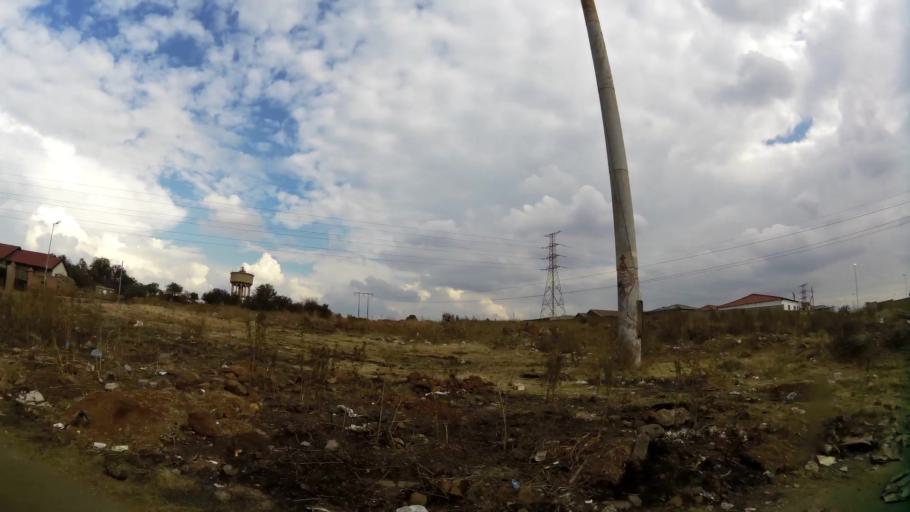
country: ZA
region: Gauteng
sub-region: City of Johannesburg Metropolitan Municipality
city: Soweto
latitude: -26.2422
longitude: 27.8593
